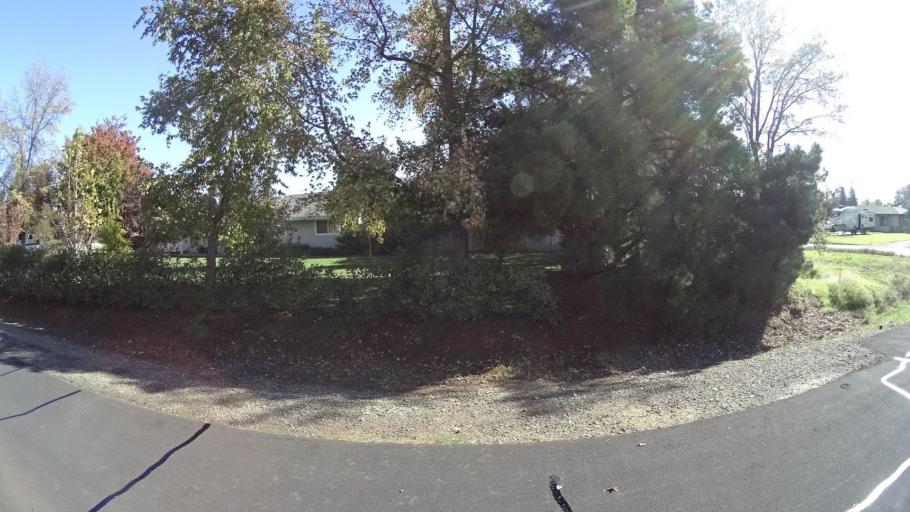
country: US
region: California
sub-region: Sacramento County
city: Wilton
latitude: 38.4434
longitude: -121.2845
